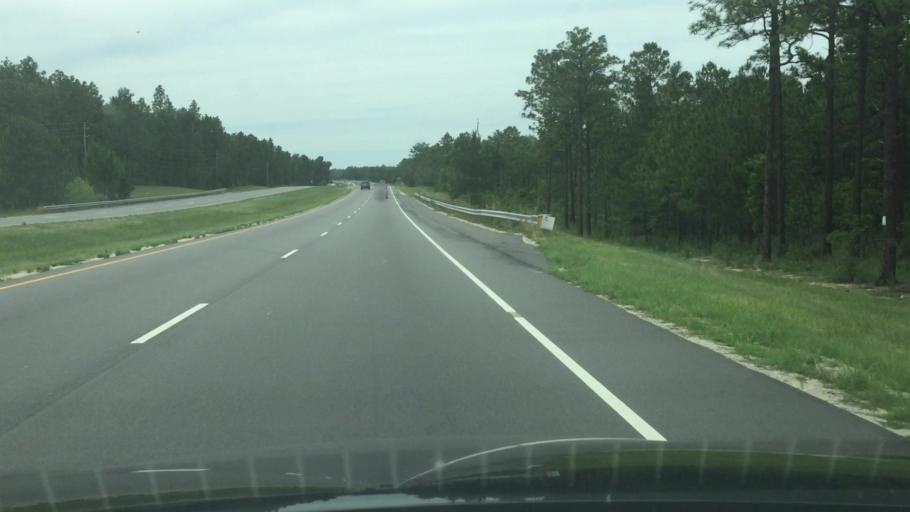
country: US
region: North Carolina
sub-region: Cumberland County
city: Spring Lake
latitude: 35.2214
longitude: -79.0052
